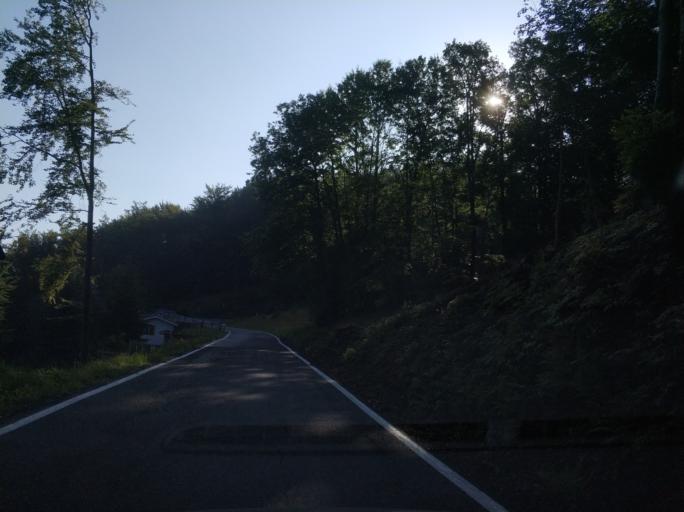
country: IT
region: Piedmont
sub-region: Provincia di Torino
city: Viu
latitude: 45.2244
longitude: 7.3902
